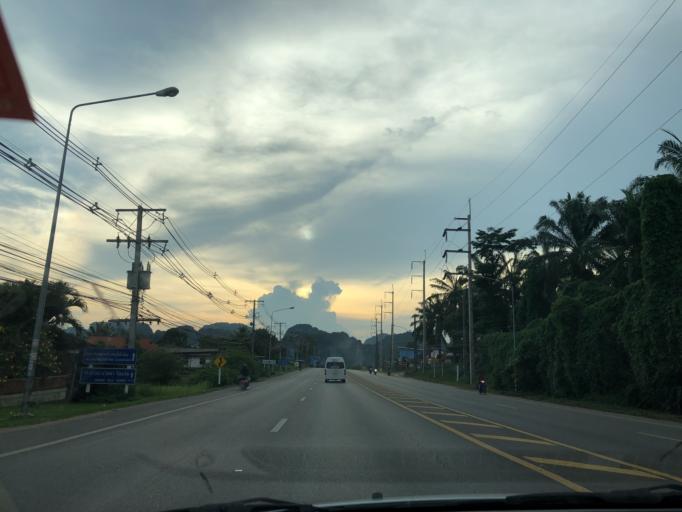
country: TH
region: Krabi
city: Krabi
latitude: 8.0831
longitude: 98.8904
